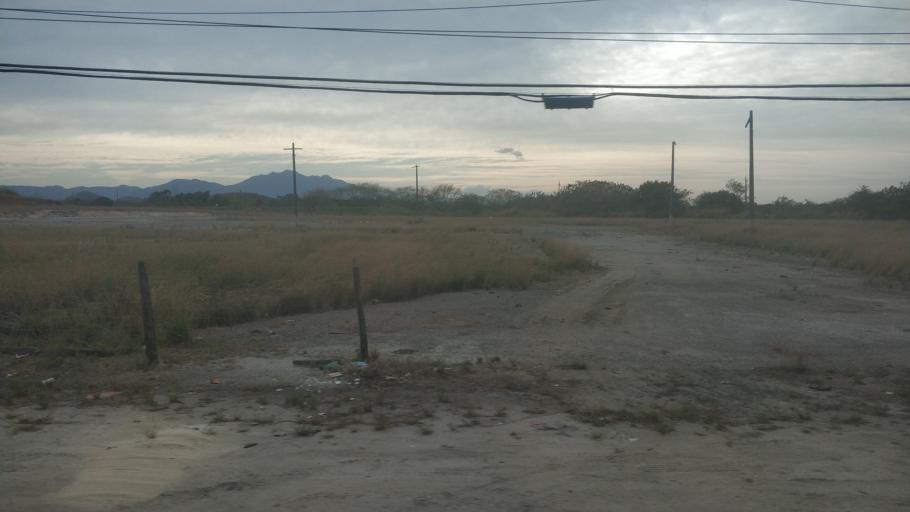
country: BR
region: Rio de Janeiro
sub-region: Seropedica
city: Seropedica
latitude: -22.7864
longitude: -43.6551
